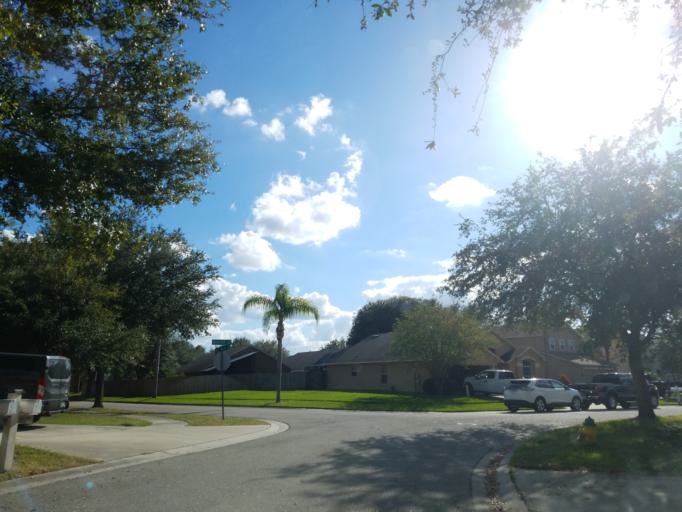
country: US
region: Florida
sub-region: Hillsborough County
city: Progress Village
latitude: 27.8840
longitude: -82.3456
